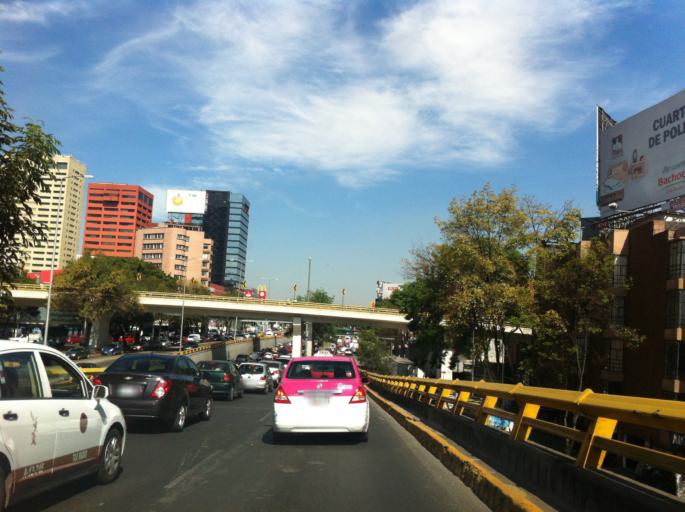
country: MX
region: Mexico City
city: Cuauhtemoc
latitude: 19.4328
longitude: -99.1718
